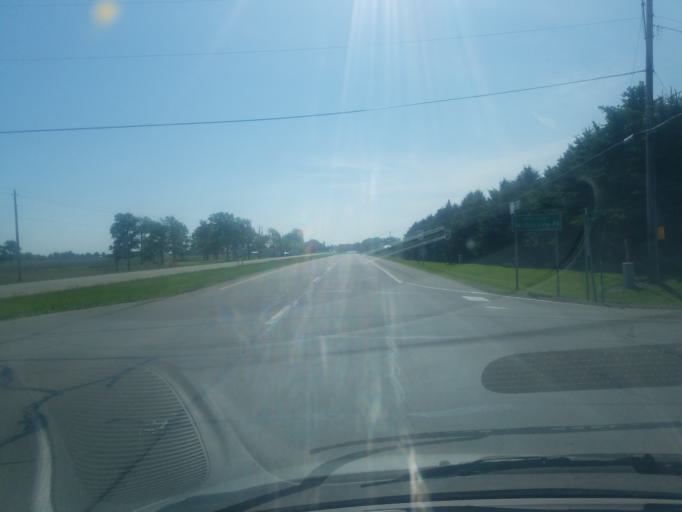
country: US
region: Ohio
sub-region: Huron County
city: Bellevue
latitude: 41.2651
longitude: -82.7895
